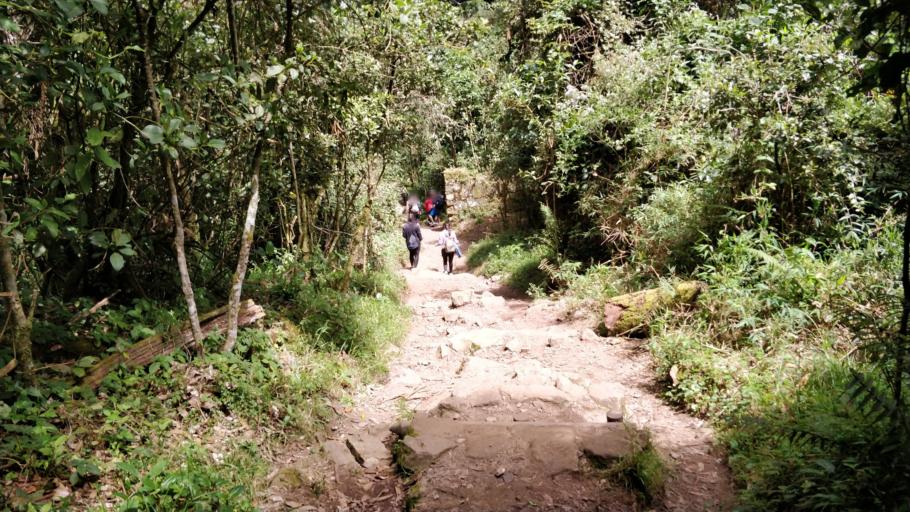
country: CO
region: Bogota D.C.
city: Barrio San Luis
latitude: 4.6450
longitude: -74.0435
